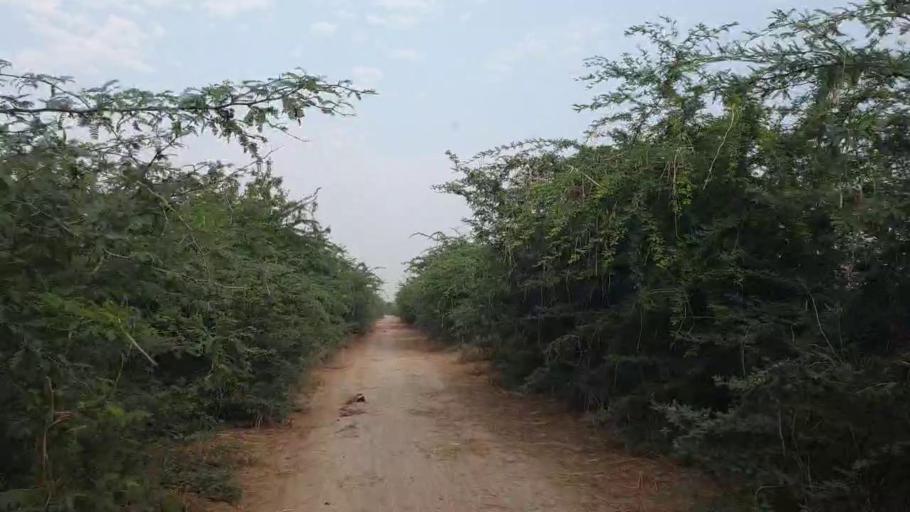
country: PK
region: Sindh
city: Tando Bago
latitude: 24.7780
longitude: 68.8922
